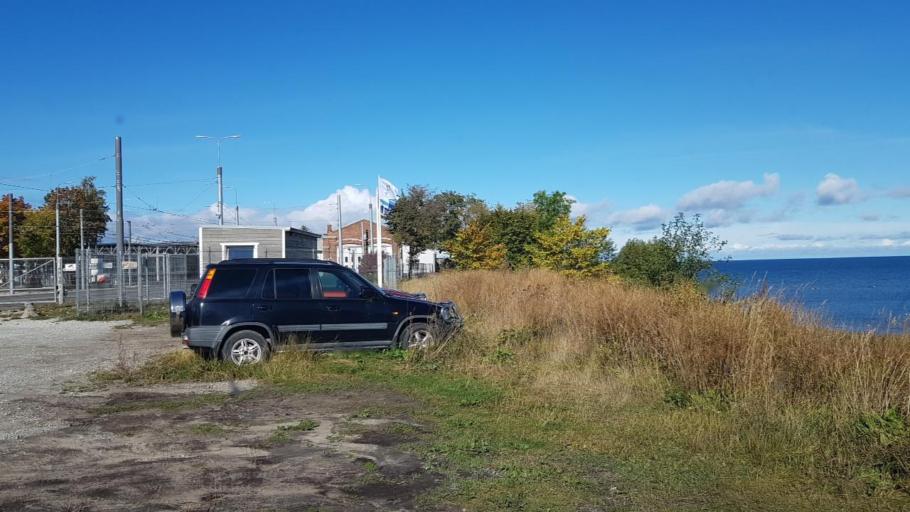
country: EE
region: Harju
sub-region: Tallinna linn
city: Tallinn
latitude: 59.4622
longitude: 24.6680
